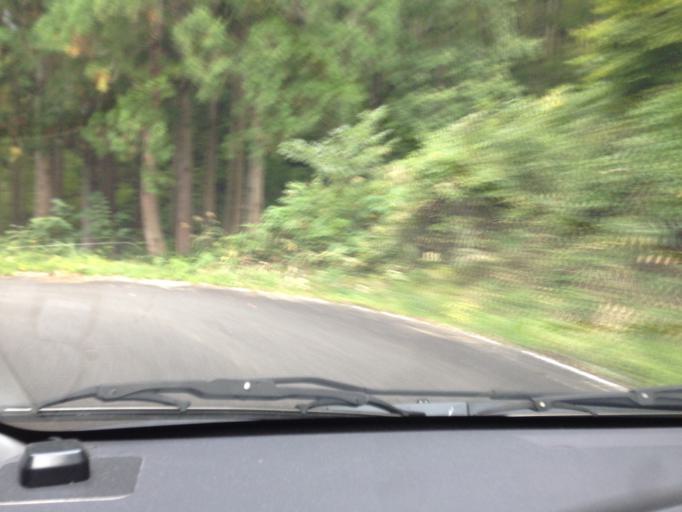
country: JP
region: Fukushima
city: Kitakata
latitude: 37.3545
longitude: 139.6007
